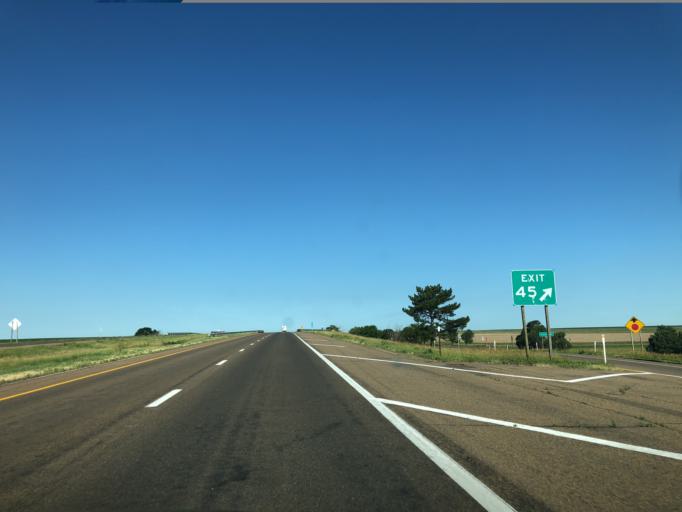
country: US
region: Kansas
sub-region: Thomas County
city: Colby
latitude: 39.3662
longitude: -101.2010
